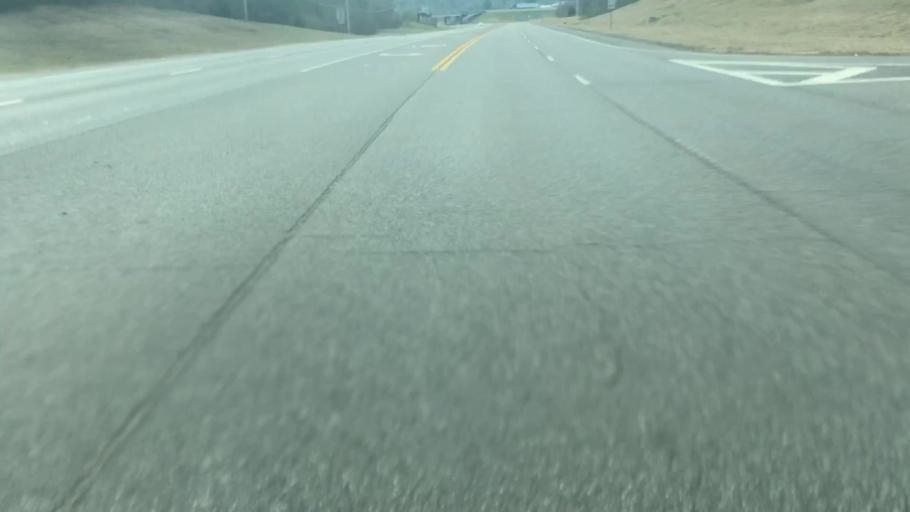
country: US
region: Alabama
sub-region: Walker County
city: Jasper
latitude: 33.7997
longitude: -87.2369
